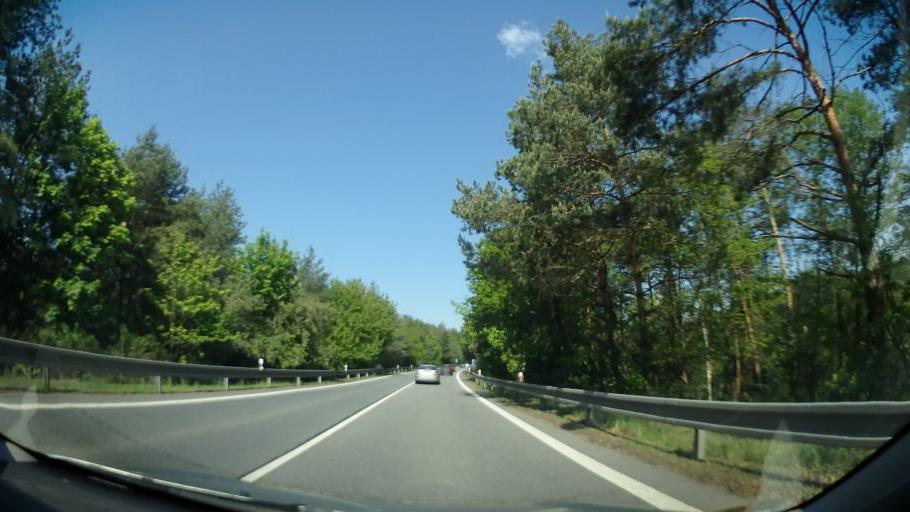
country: CZ
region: South Moravian
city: Zbraslav
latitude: 49.1775
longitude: 16.3026
